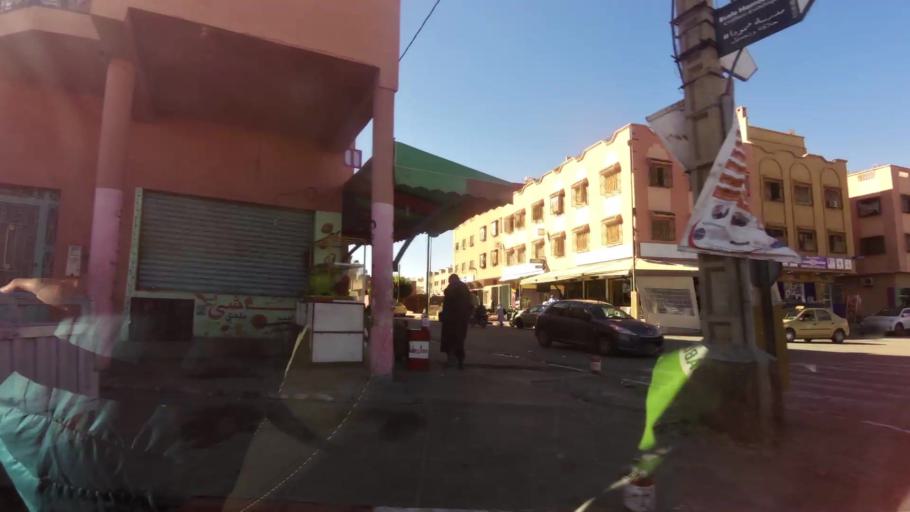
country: MA
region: Marrakech-Tensift-Al Haouz
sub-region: Marrakech
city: Marrakesh
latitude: 31.5977
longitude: -8.0360
